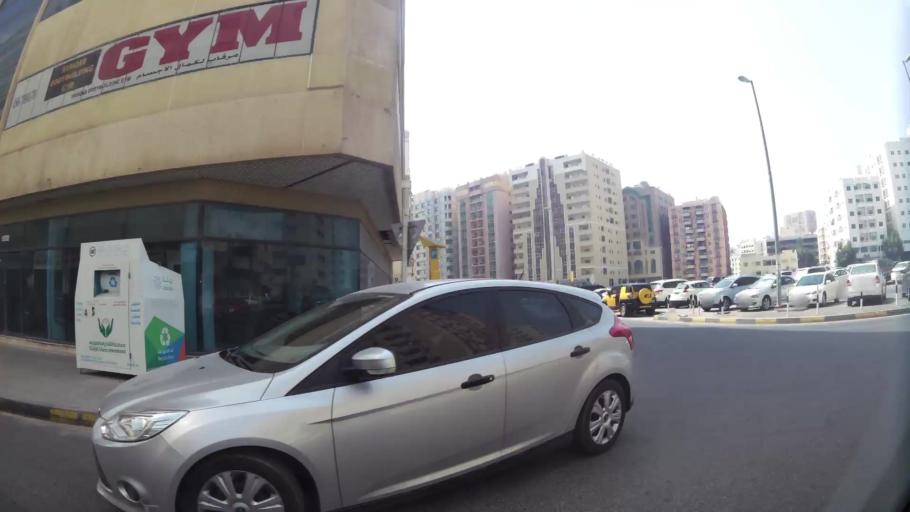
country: AE
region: Ash Shariqah
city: Sharjah
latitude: 25.3503
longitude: 55.3888
